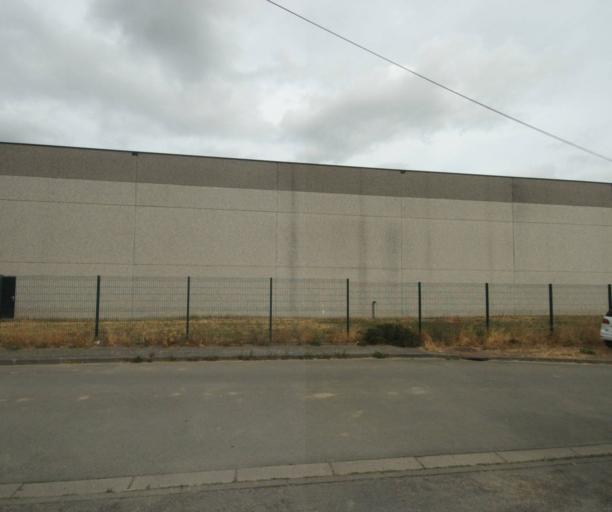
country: FR
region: Nord-Pas-de-Calais
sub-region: Departement du Nord
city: Linselles
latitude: 50.7474
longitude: 3.0892
